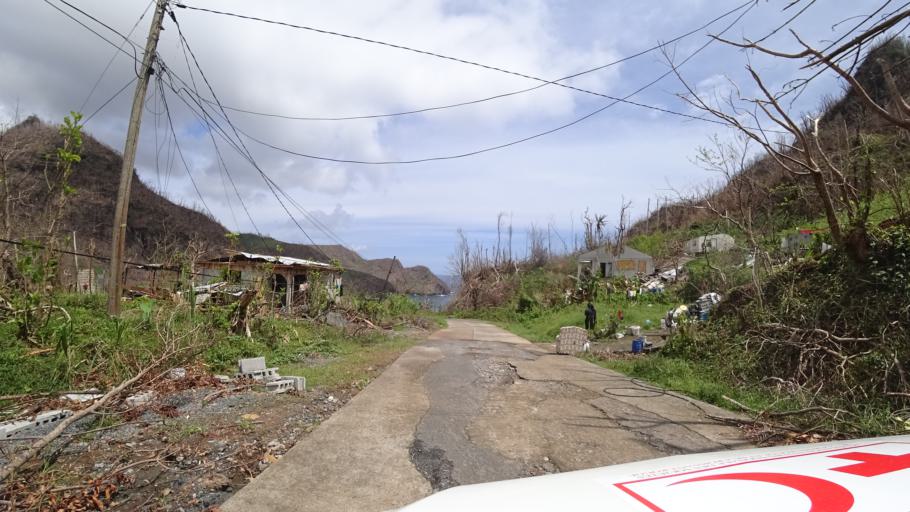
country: DM
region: Saint David
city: Rosalie
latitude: 15.3986
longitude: -61.2581
